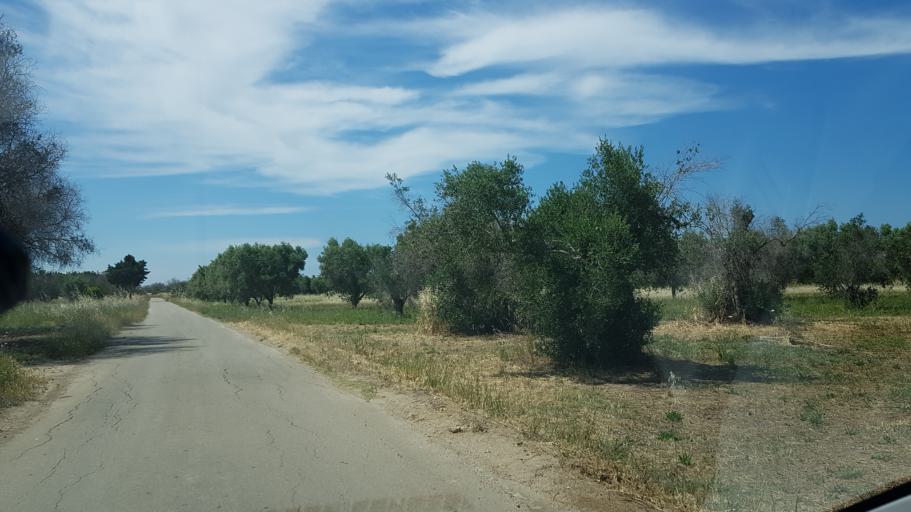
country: IT
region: Apulia
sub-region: Provincia di Brindisi
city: San Pietro Vernotico
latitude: 40.5276
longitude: 18.0057
